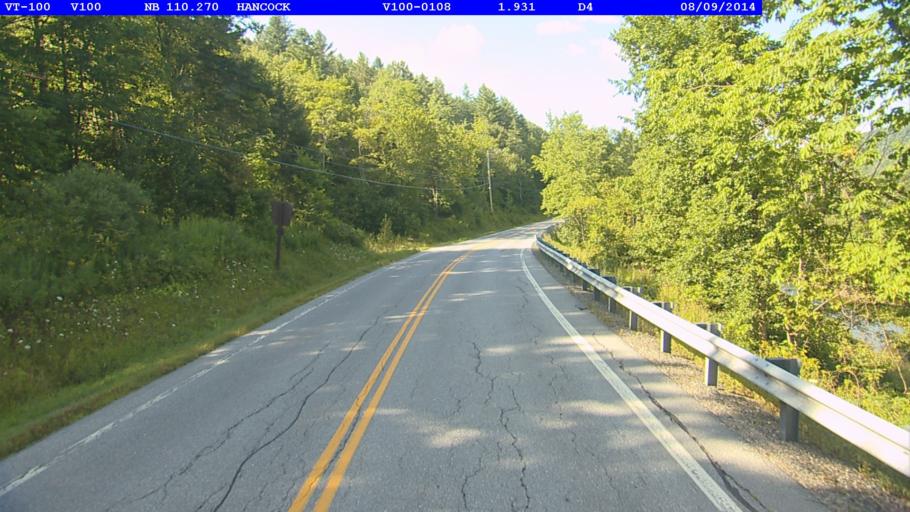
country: US
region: Vermont
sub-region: Orange County
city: Randolph
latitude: 43.9366
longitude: -72.8425
